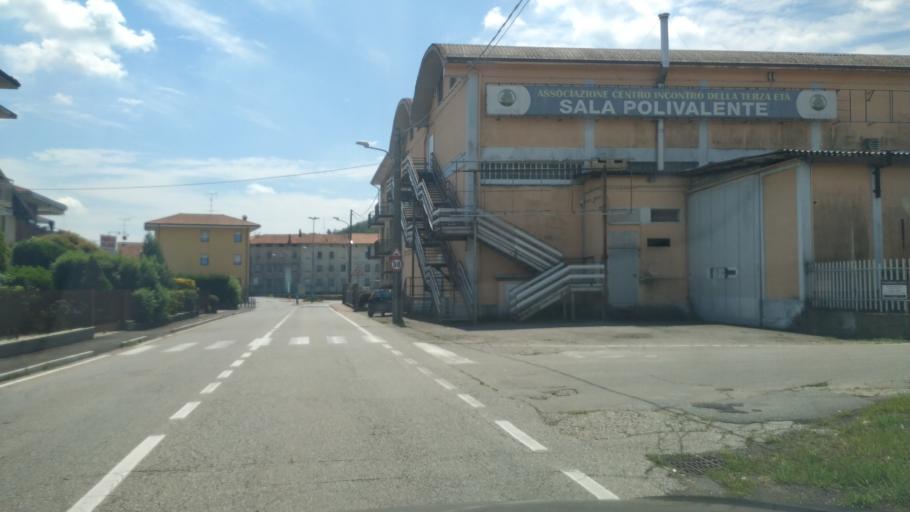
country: IT
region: Piedmont
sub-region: Provincia di Novara
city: Borgomanero
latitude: 45.7008
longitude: 8.4479
